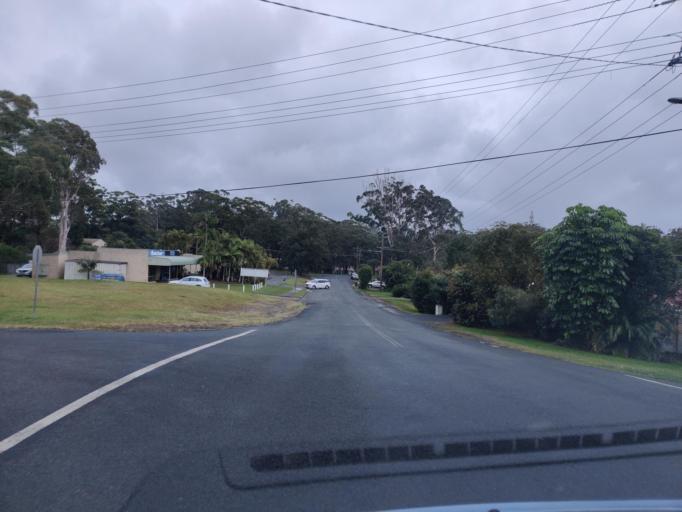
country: AU
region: New South Wales
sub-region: Great Lakes
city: Forster
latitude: -32.3822
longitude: 152.5029
